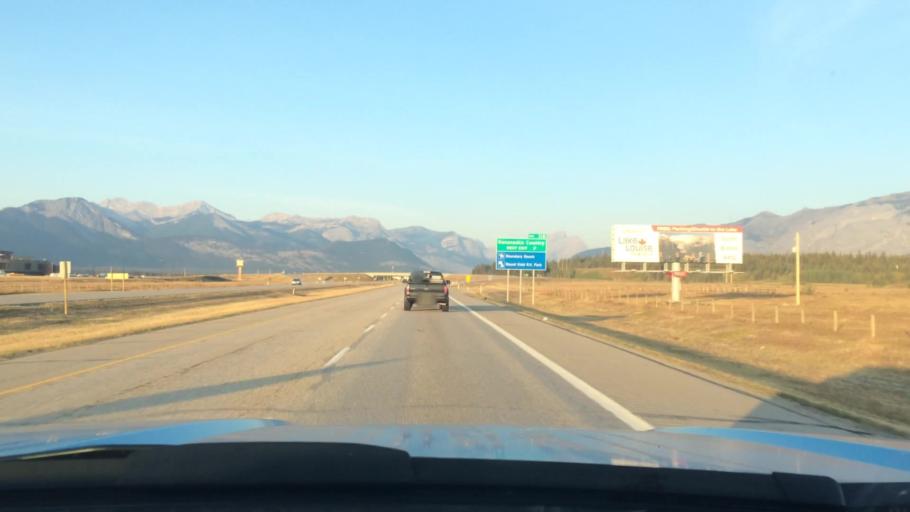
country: CA
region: Alberta
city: Canmore
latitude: 51.1083
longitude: -115.0098
